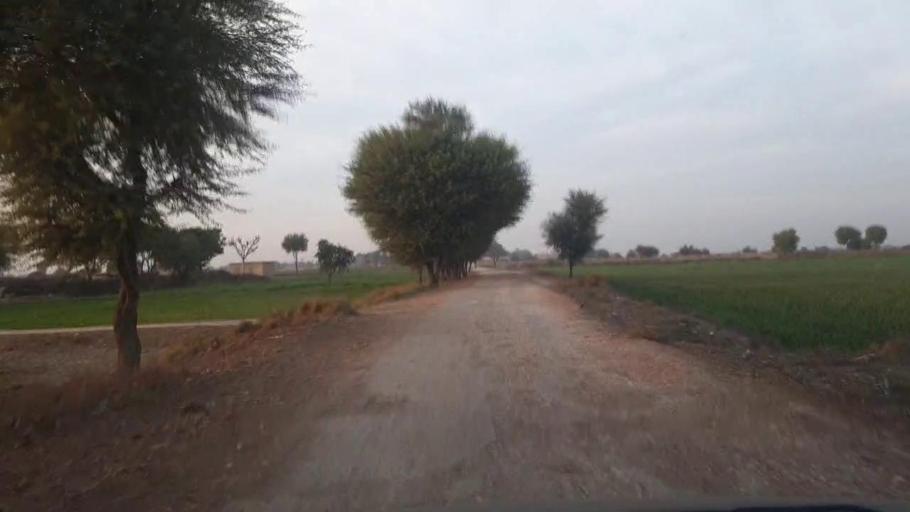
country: PK
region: Sindh
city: Shahpur Chakar
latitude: 26.0700
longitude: 68.5327
